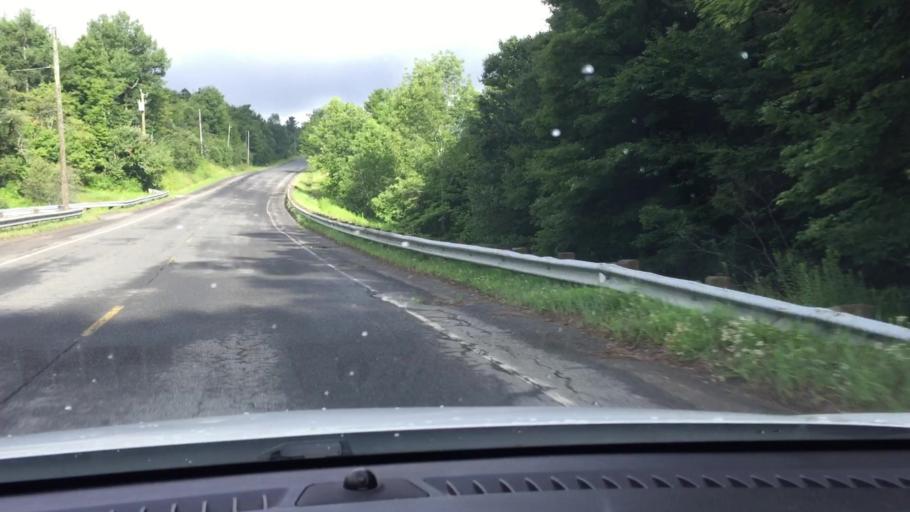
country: US
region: Massachusetts
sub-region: Berkshire County
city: Hinsdale
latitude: 42.4330
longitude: -73.0211
